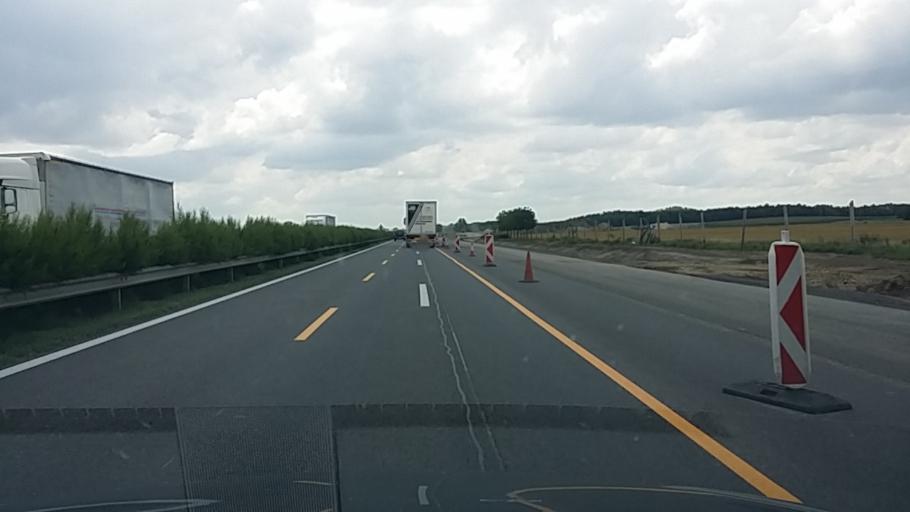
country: HU
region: Bacs-Kiskun
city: Lajosmizse
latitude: 46.9674
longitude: 19.6152
